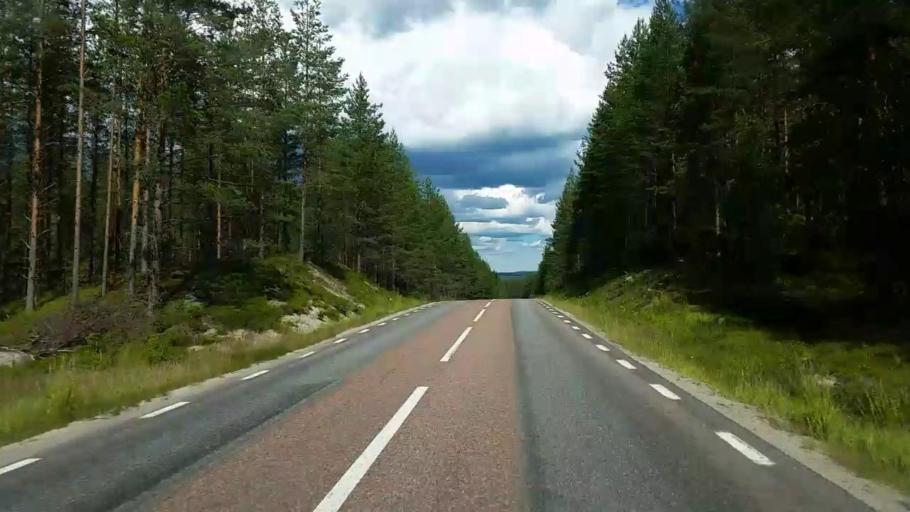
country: SE
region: Gaevleborg
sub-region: Ovanakers Kommun
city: Edsbyn
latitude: 61.3239
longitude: 15.5173
